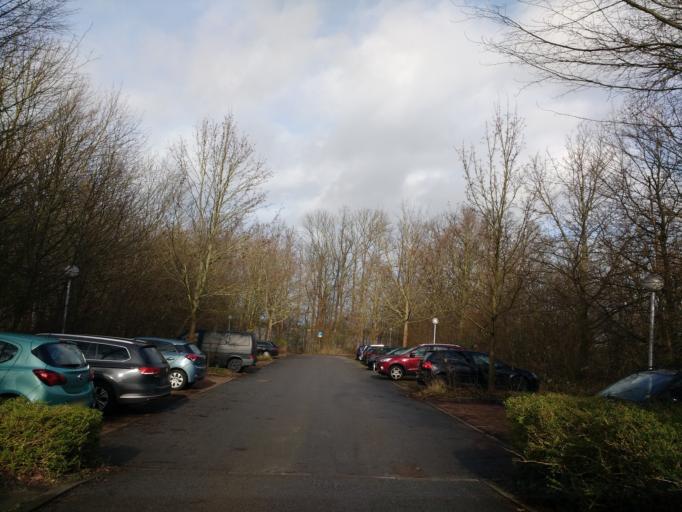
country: DE
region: Schleswig-Holstein
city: Heiligenhafen
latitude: 54.3743
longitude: 10.9599
